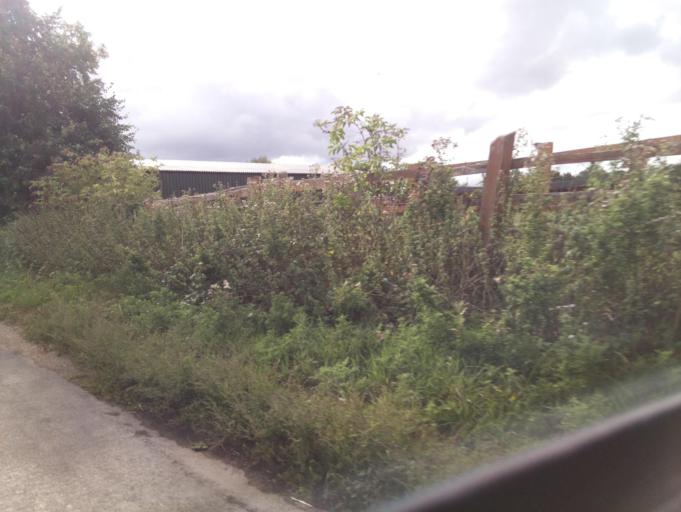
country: GB
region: England
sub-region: Leicestershire
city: Loughborough
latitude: 52.7921
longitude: -1.1963
